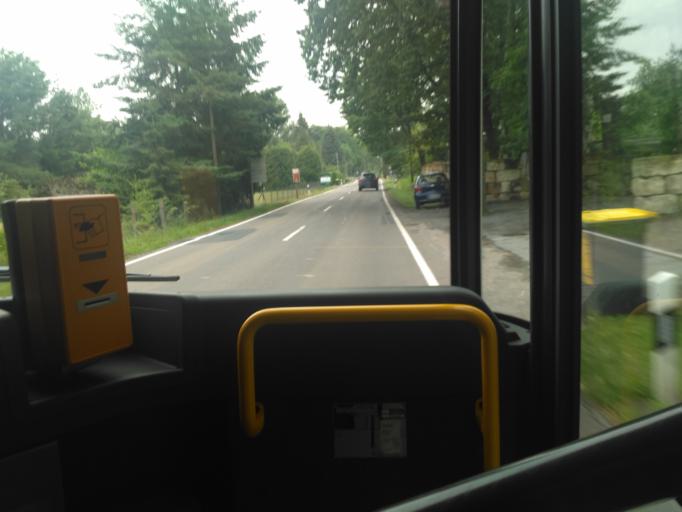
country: DE
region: Saxony
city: Weinbohla
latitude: 51.1629
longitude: 13.5978
